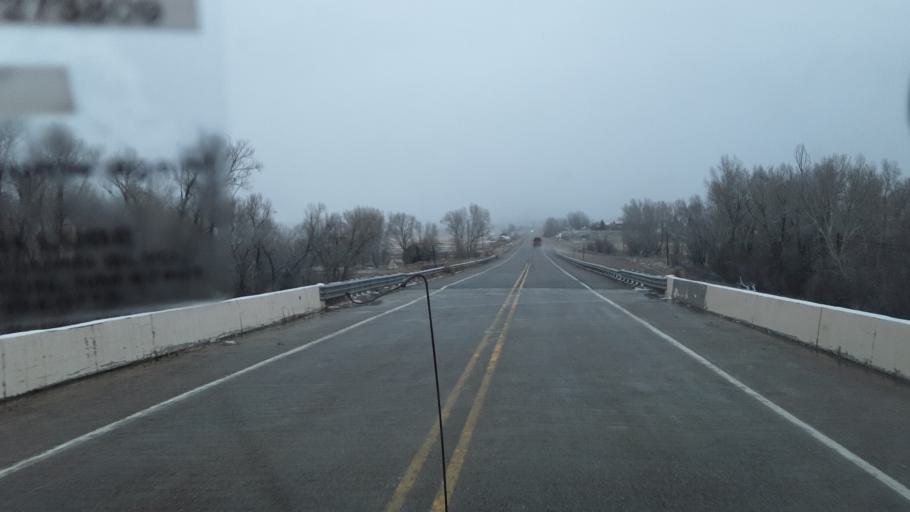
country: US
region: New Mexico
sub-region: Rio Arriba County
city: Tierra Amarilla
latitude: 36.7465
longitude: -106.5675
